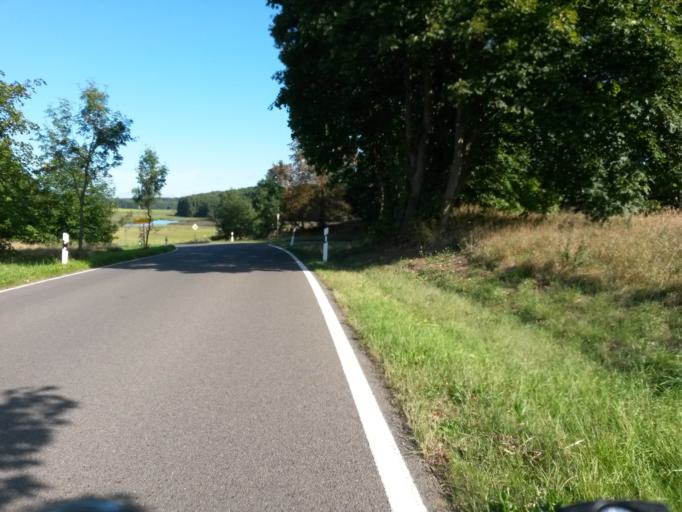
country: DE
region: Brandenburg
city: Lychen
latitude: 53.1304
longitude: 13.3849
